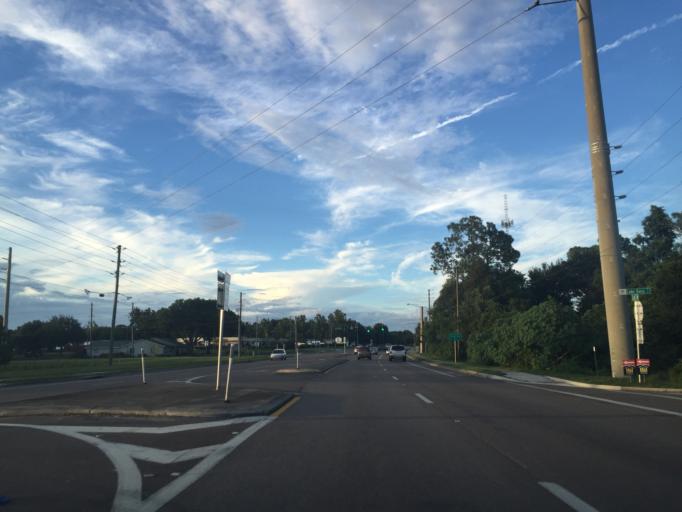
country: US
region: Florida
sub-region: Lake County
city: Tavares
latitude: 28.7882
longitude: -81.7473
